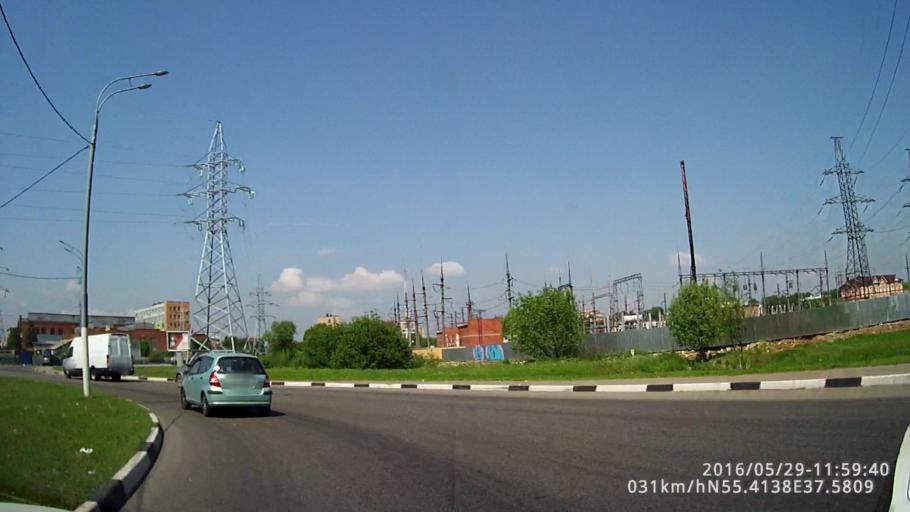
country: RU
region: Moskovskaya
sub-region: Podol'skiy Rayon
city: Podol'sk
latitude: 55.4140
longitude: 37.5808
